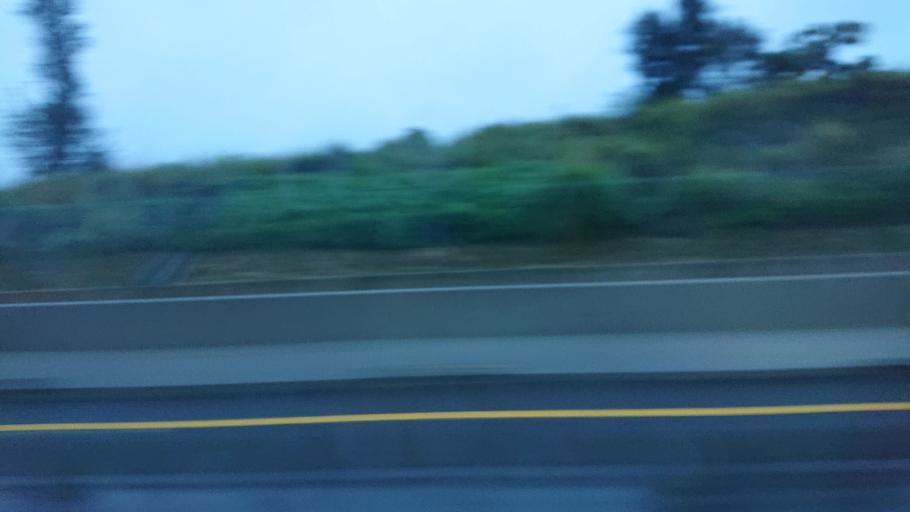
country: TW
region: Taiwan
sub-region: Miaoli
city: Miaoli
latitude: 24.5637
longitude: 120.7146
